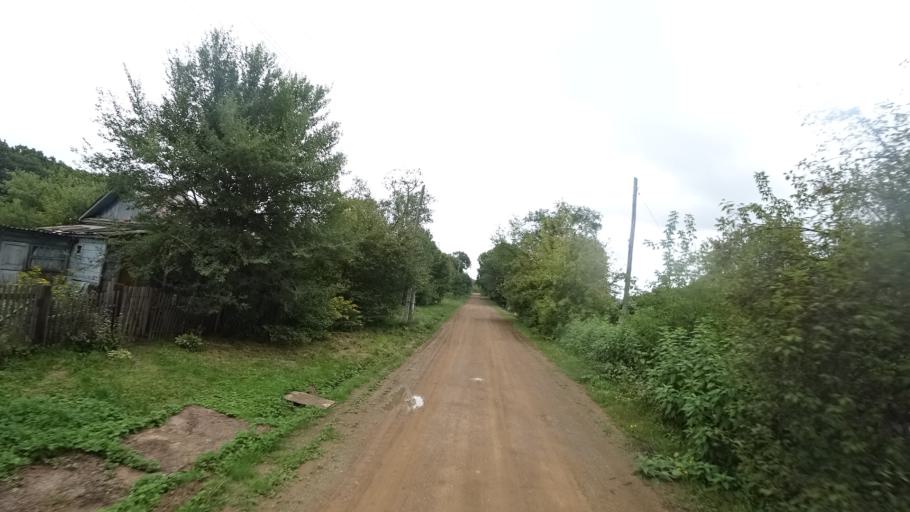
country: RU
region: Primorskiy
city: Chernigovka
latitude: 44.4406
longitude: 132.5742
